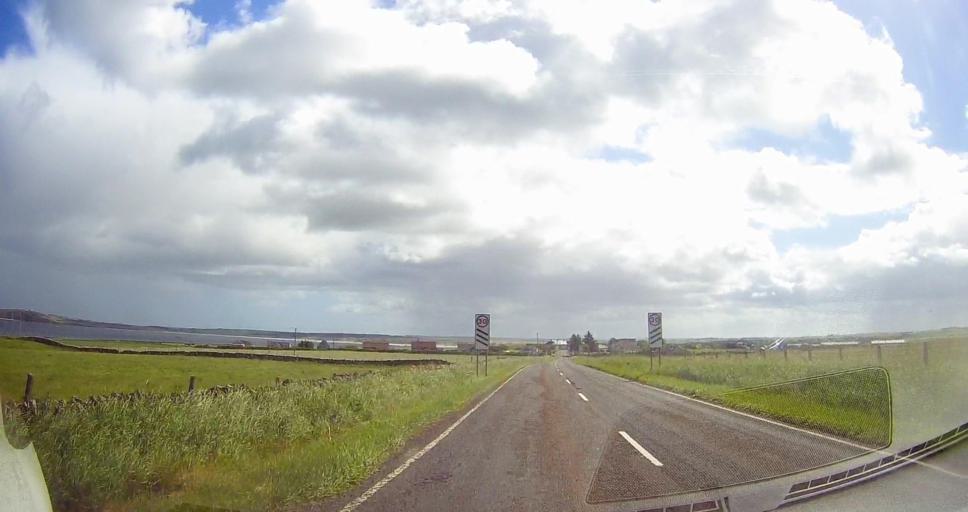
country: GB
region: Scotland
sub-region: Highland
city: Thurso
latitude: 58.5955
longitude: -3.4099
